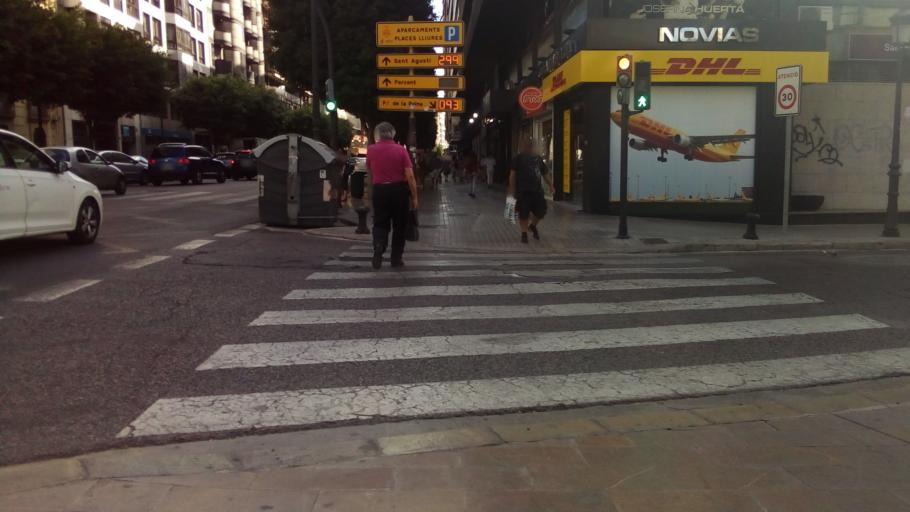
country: ES
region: Valencia
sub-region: Provincia de Valencia
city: Valencia
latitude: 39.4717
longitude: -0.3690
